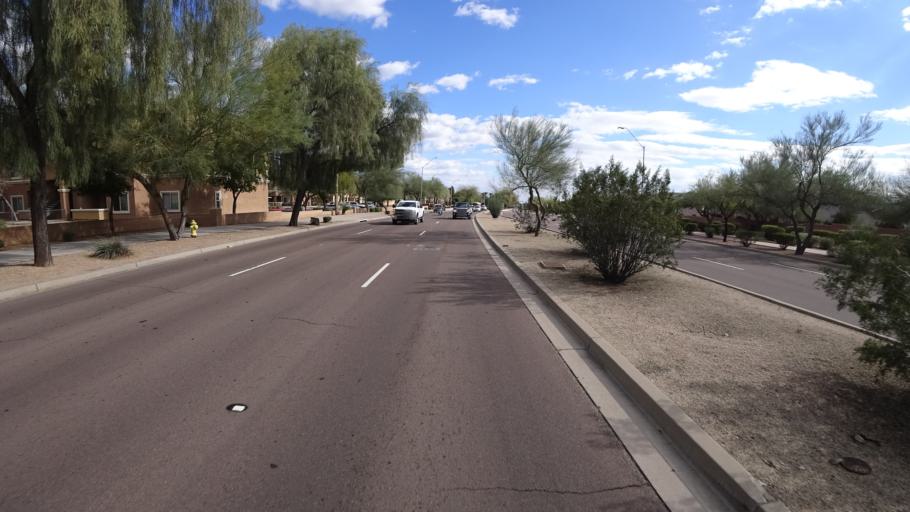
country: US
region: Arizona
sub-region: Maricopa County
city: Paradise Valley
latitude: 33.6282
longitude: -111.8811
